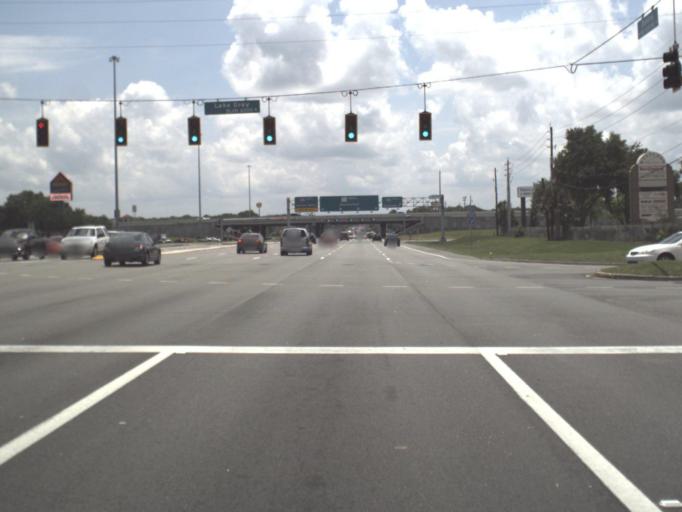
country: US
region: Florida
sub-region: Clay County
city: Bellair-Meadowbrook Terrace
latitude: 30.1999
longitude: -81.7396
